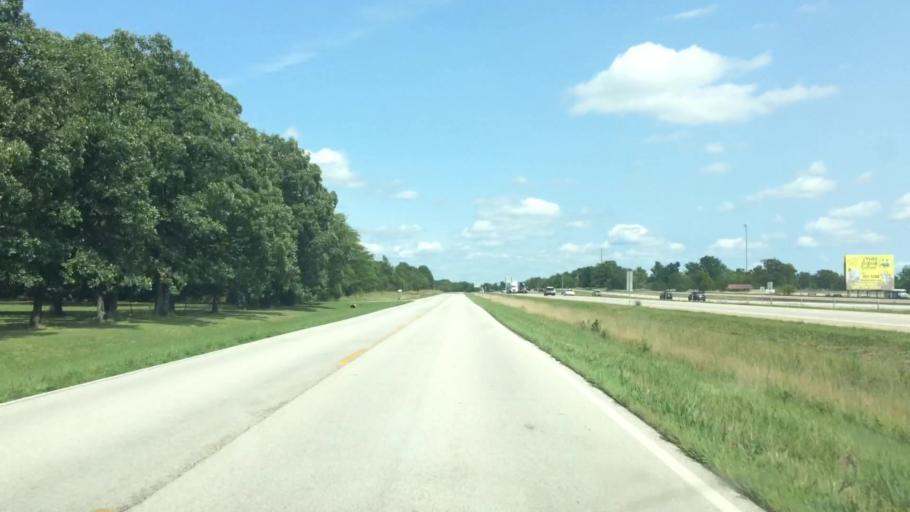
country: US
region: Missouri
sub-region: Greene County
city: Strafford
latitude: 37.2727
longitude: -93.0596
